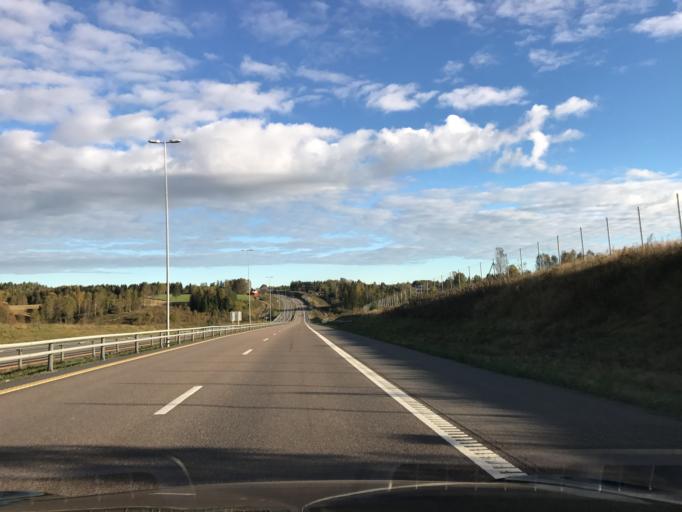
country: NO
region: Akershus
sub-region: Eidsvoll
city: Raholt
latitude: 60.2360
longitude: 11.1756
